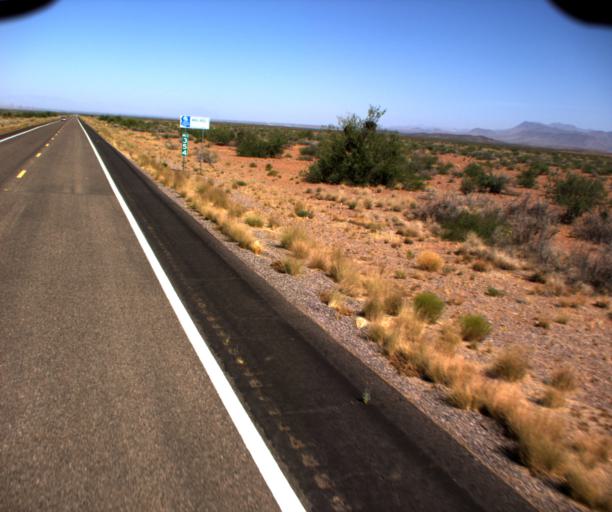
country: US
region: Arizona
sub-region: Graham County
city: Safford
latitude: 32.7700
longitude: -109.4781
